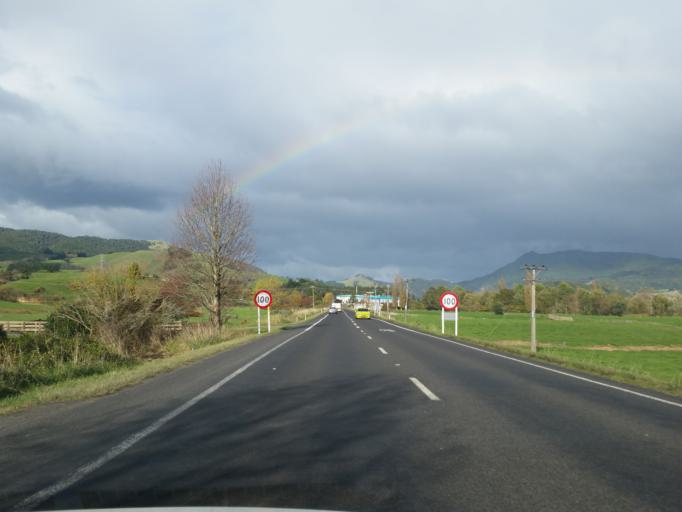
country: NZ
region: Waikato
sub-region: Hauraki District
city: Paeroa
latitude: -37.3869
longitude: 175.6802
